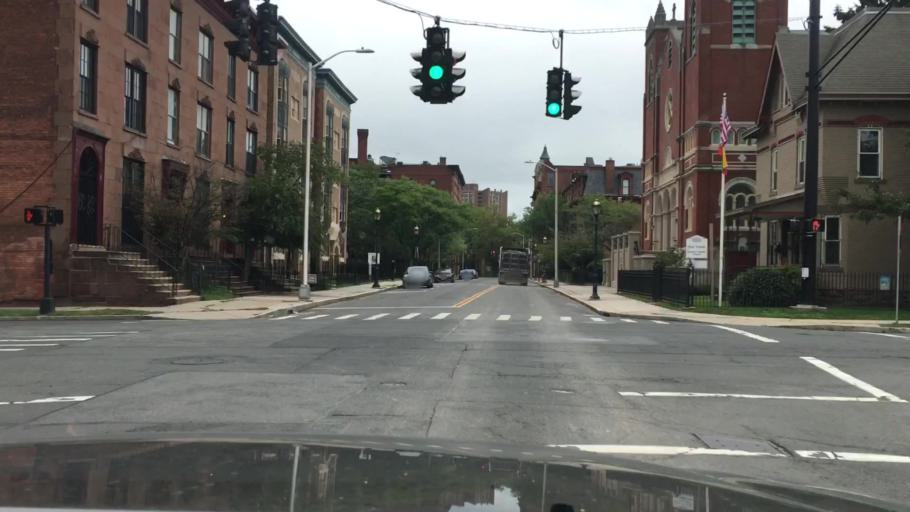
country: US
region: Connecticut
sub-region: Hartford County
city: Hartford
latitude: 41.7614
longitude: -72.6772
